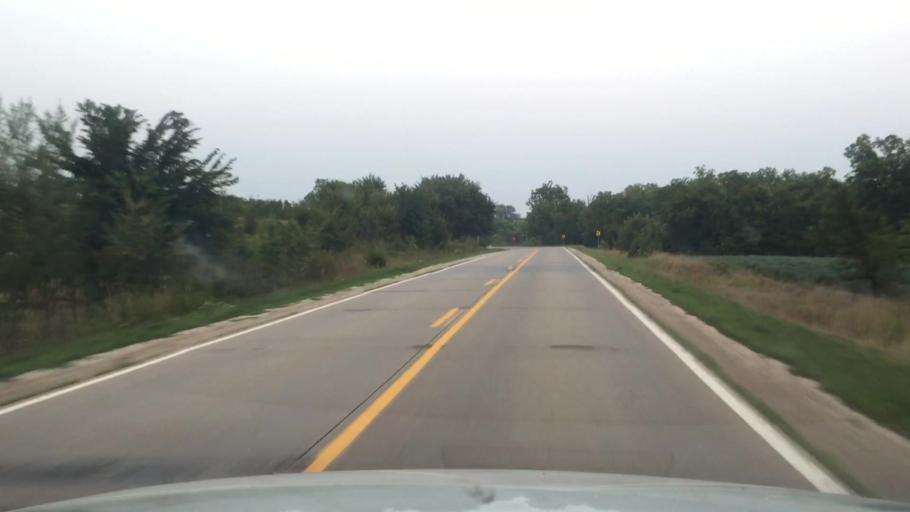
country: US
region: Iowa
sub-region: Clarke County
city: Osceola
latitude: 41.1802
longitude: -93.7147
